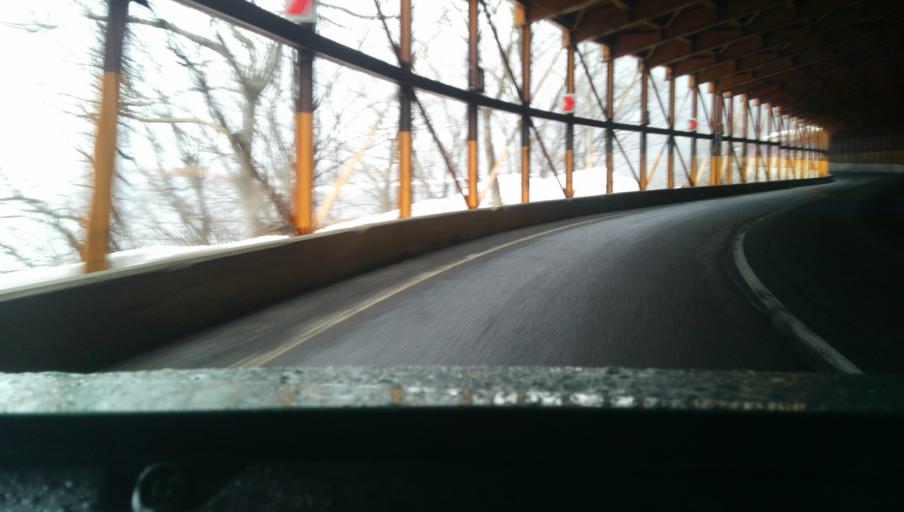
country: JP
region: Iwate
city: Kitakami
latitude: 39.3090
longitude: 140.8444
